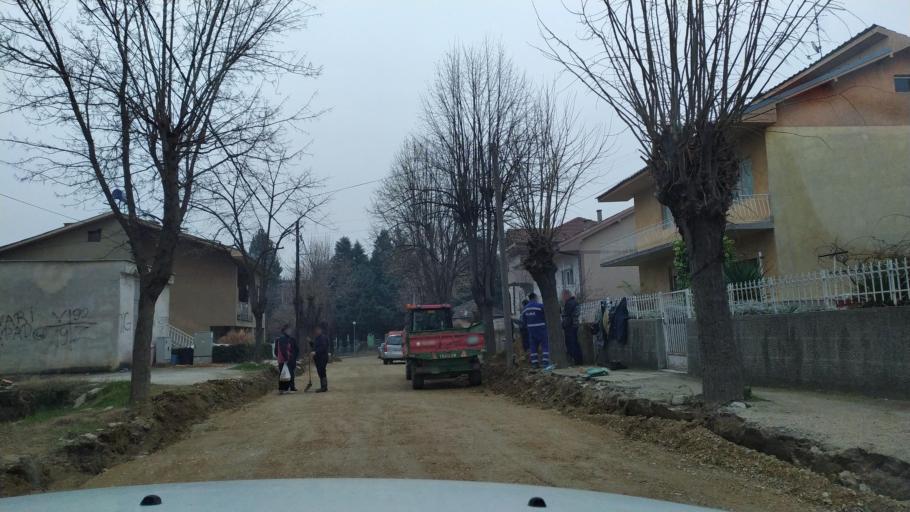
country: MK
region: Negotino
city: Negotino
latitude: 41.4817
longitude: 22.0825
